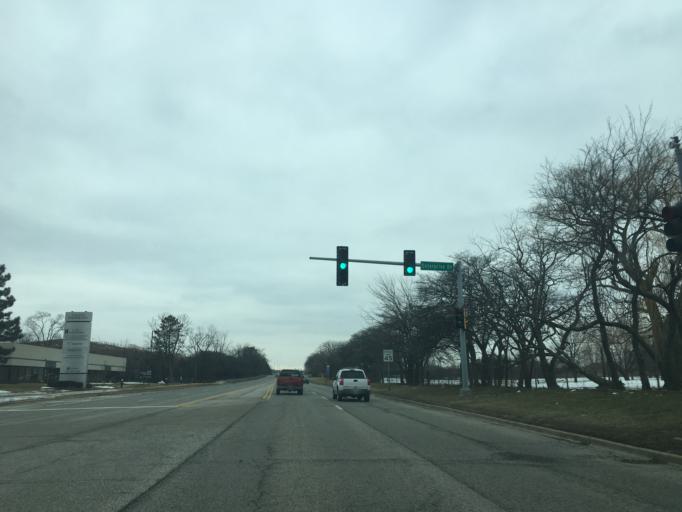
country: US
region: Illinois
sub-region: DuPage County
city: Oak Brook
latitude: 41.8480
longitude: -87.9096
